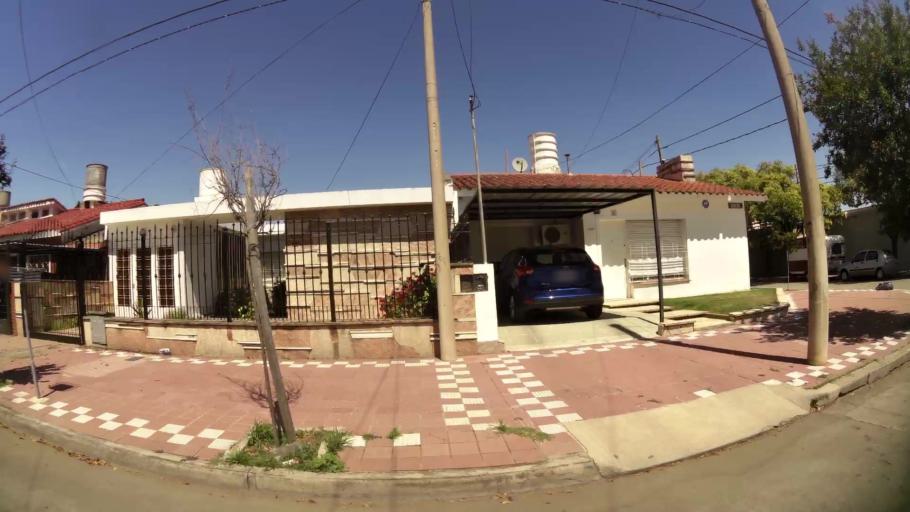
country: AR
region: Cordoba
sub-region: Departamento de Capital
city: Cordoba
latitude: -31.3819
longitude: -64.1584
